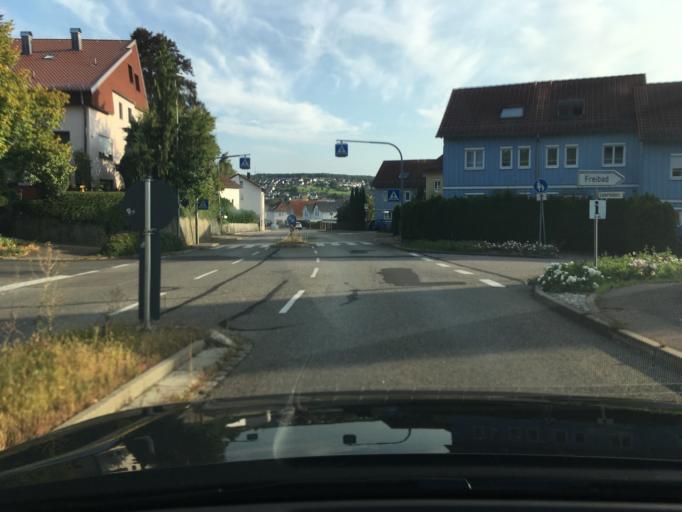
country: DE
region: Baden-Wuerttemberg
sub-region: Regierungsbezirk Stuttgart
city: Uhingen
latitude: 48.7134
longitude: 9.5799
